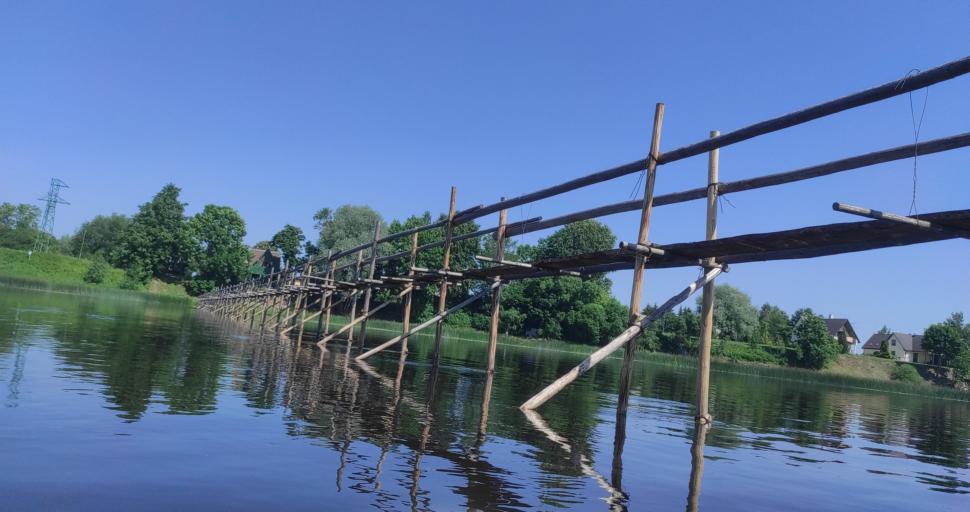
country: LV
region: Salacgrivas
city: Salacgriva
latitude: 57.7524
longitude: 24.3747
